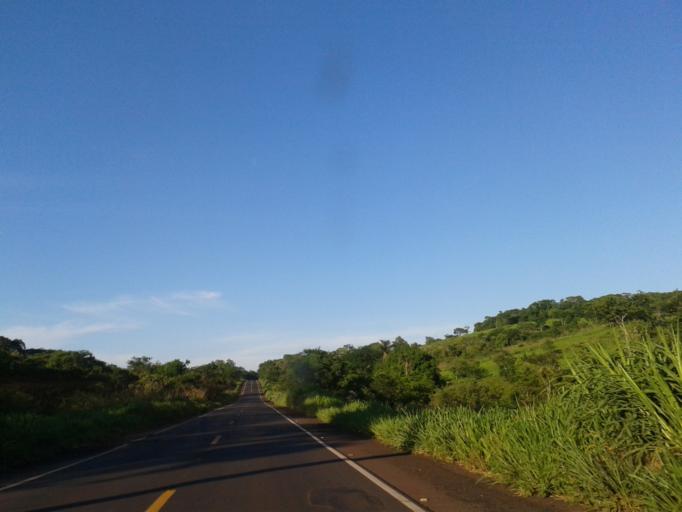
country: BR
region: Minas Gerais
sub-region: Santa Vitoria
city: Santa Vitoria
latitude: -18.9371
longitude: -49.8037
